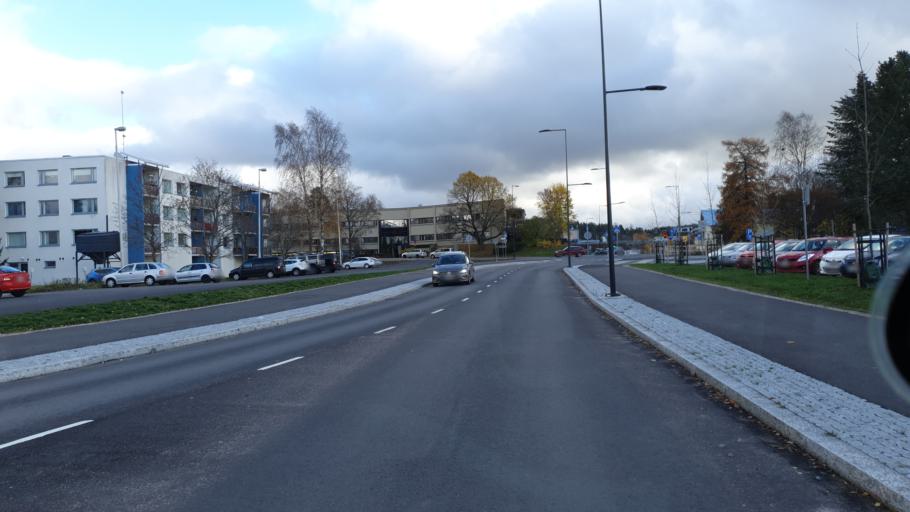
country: FI
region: Uusimaa
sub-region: Helsinki
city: Kirkkonummi
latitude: 60.1203
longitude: 24.4359
